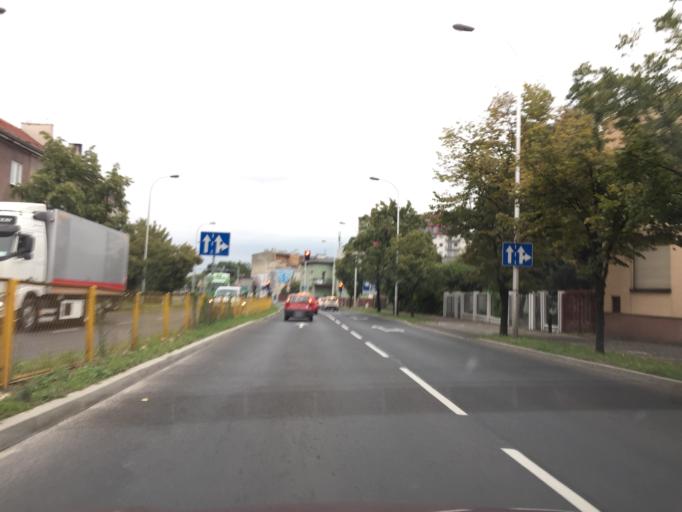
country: PL
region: Greater Poland Voivodeship
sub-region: Kalisz
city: Kalisz
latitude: 51.7569
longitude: 18.0741
